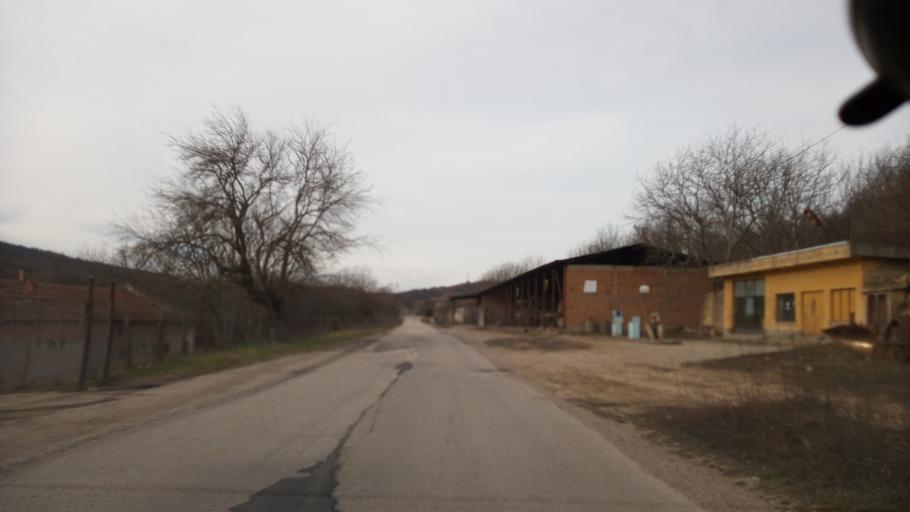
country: BG
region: Pleven
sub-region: Obshtina Belene
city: Belene
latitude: 43.6113
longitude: 25.0157
